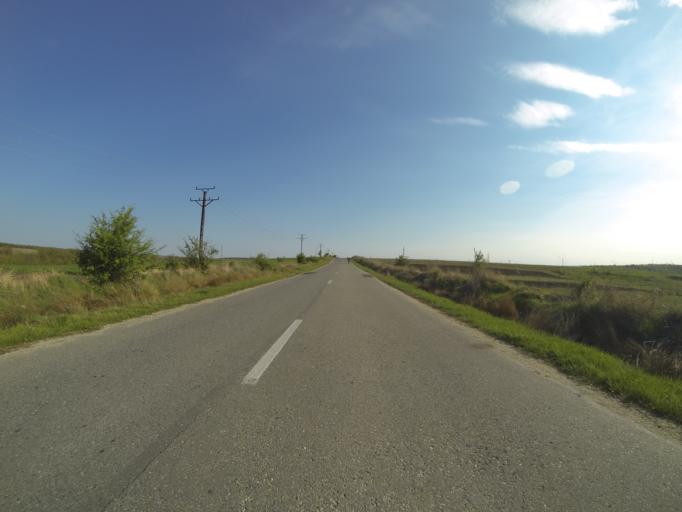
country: RO
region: Dolj
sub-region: Comuna Filiasi
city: Fratostita
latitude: 44.5800
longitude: 23.5887
